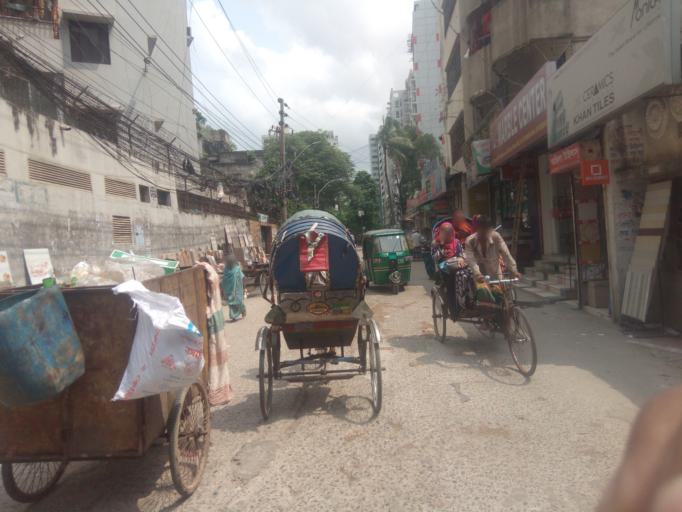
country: BD
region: Dhaka
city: Azimpur
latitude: 23.7448
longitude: 90.3930
